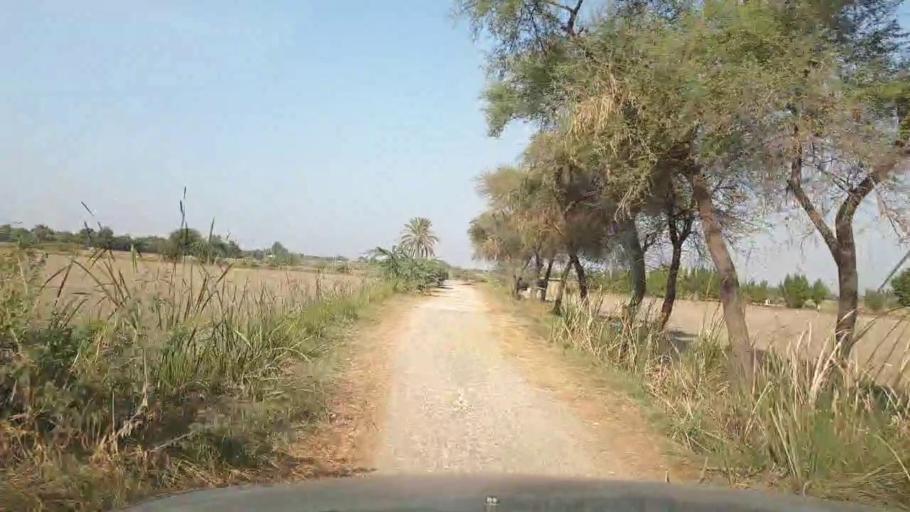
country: PK
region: Sindh
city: Tando Muhammad Khan
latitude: 25.0921
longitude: 68.5751
